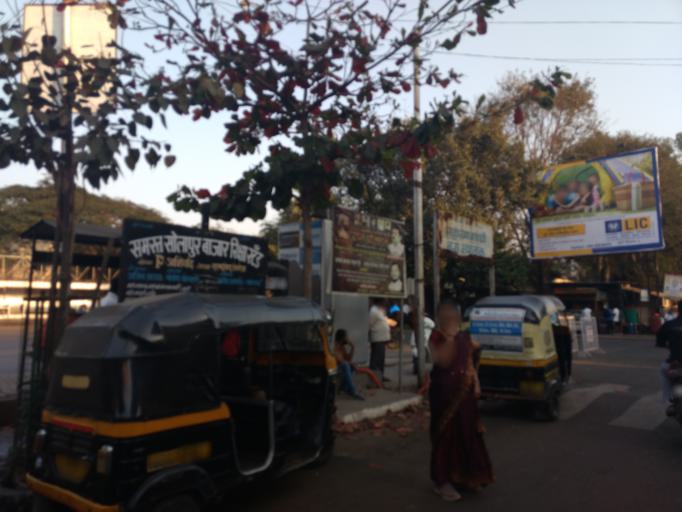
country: IN
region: Maharashtra
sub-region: Pune Division
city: Pune
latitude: 18.5059
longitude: 73.8820
